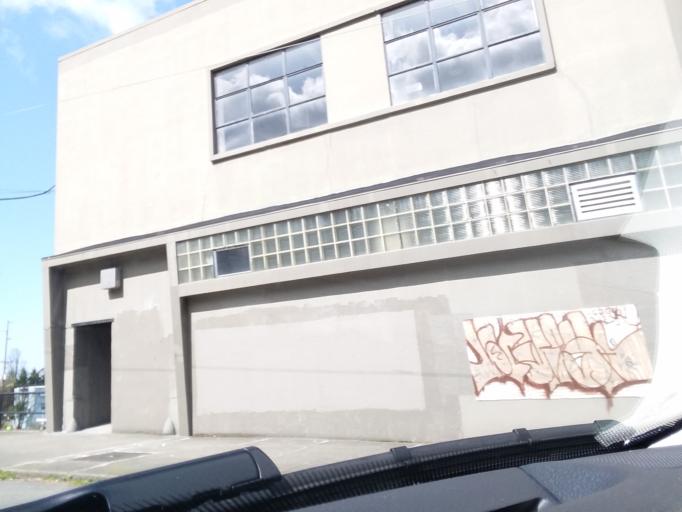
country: US
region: Washington
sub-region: King County
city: Seattle
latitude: 47.6304
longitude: -122.3279
